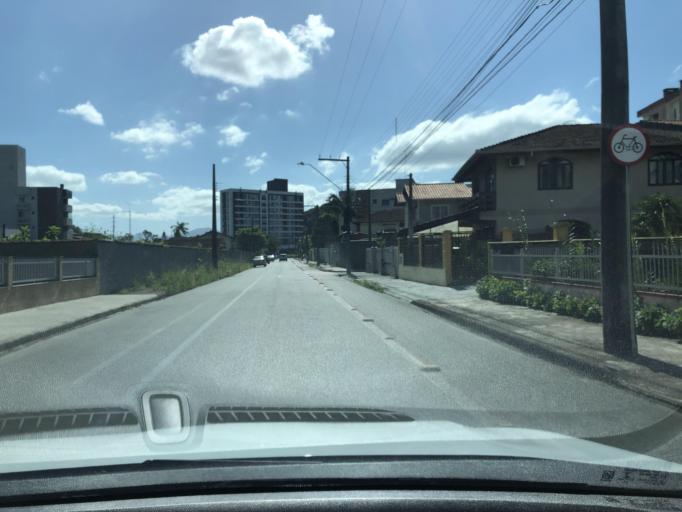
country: BR
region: Santa Catarina
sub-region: Joinville
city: Joinville
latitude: -26.2687
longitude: -48.8466
